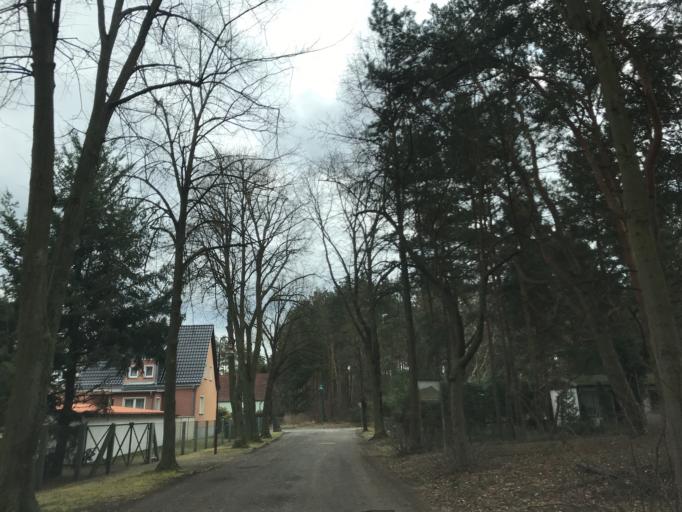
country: DE
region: Brandenburg
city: Zossen
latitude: 52.1373
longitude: 13.4709
